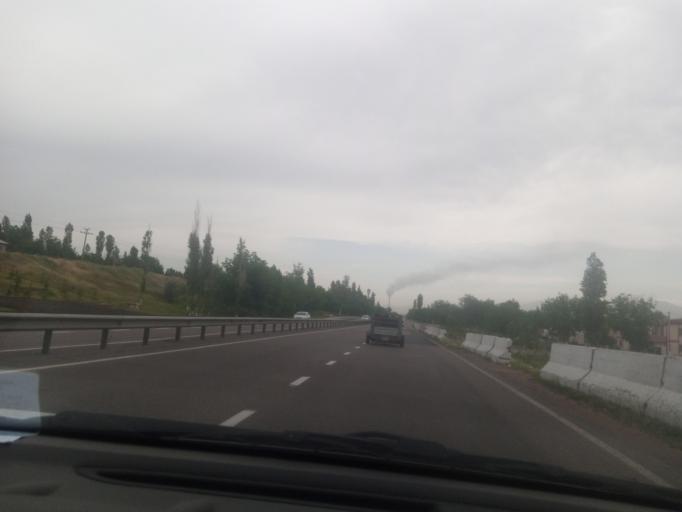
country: UZ
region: Toshkent
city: Ohangaron
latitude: 40.8993
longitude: 69.6957
